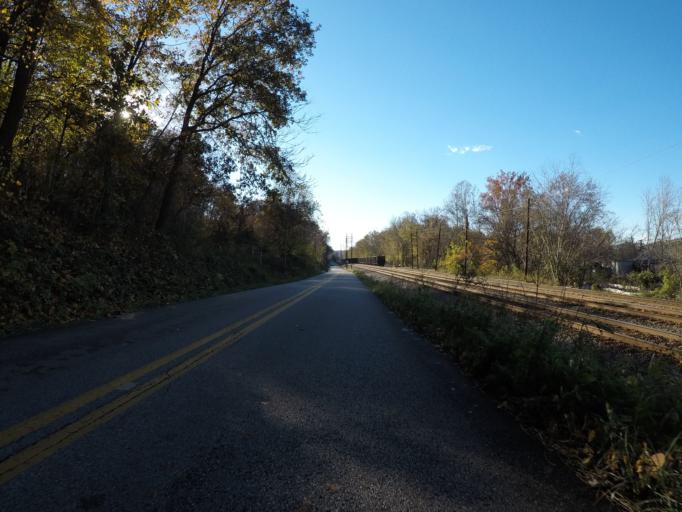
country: US
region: Ohio
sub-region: Lawrence County
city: Burlington
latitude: 38.3948
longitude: -82.5389
